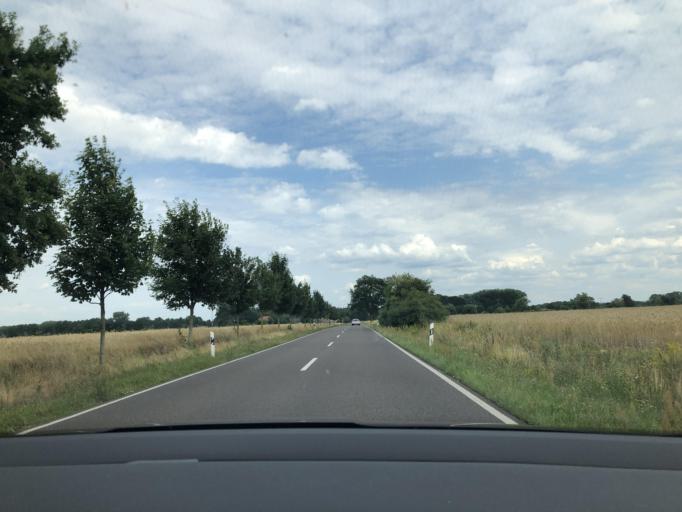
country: DE
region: Saxony-Anhalt
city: Lindau
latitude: 52.0104
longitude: 12.1954
